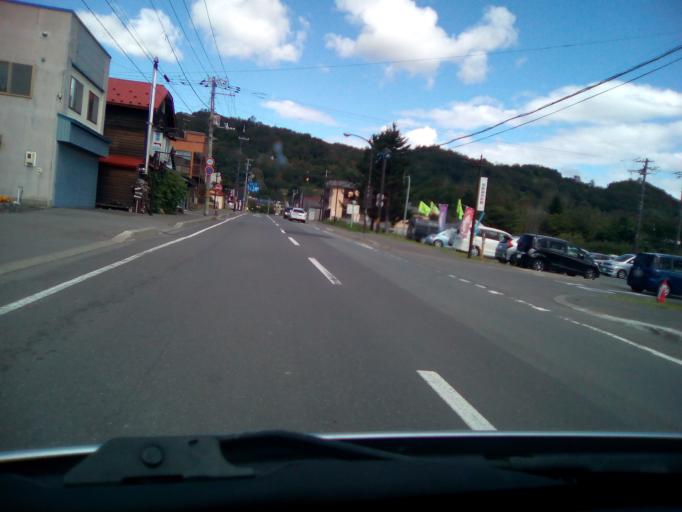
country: JP
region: Hokkaido
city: Date
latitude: 42.6470
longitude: 140.8322
